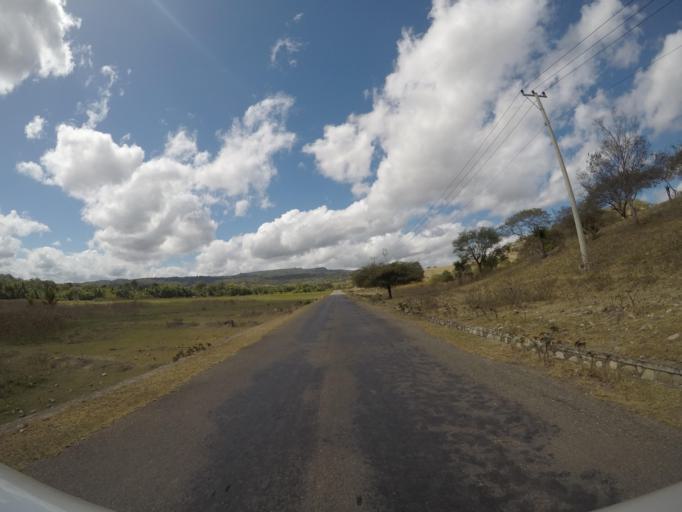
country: TL
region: Lautem
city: Lospalos
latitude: -8.4198
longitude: 126.8289
